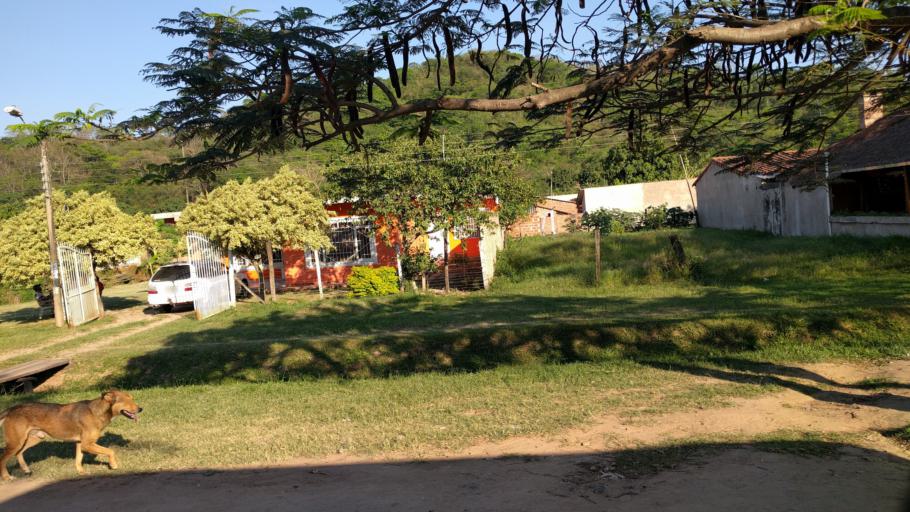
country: BO
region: Santa Cruz
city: Jorochito
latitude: -18.0579
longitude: -63.4296
